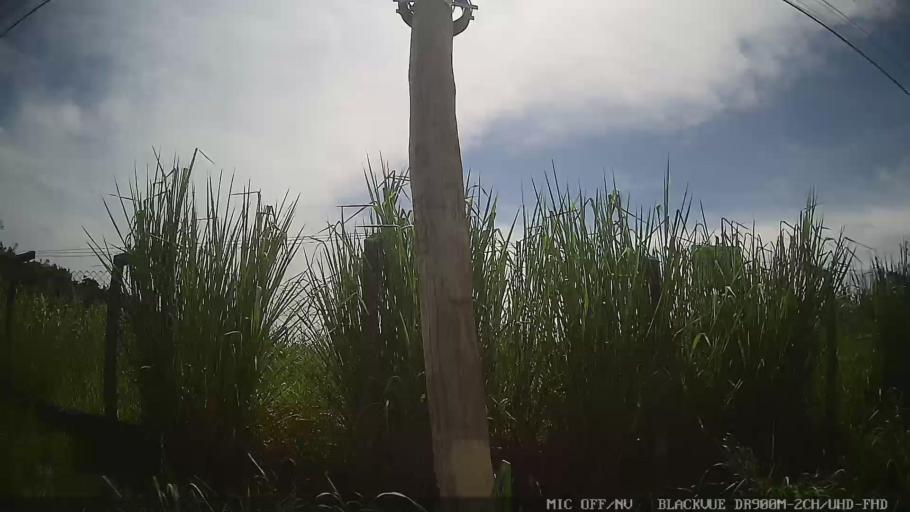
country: BR
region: Sao Paulo
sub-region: Santa Isabel
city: Santa Isabel
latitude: -23.3636
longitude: -46.1770
